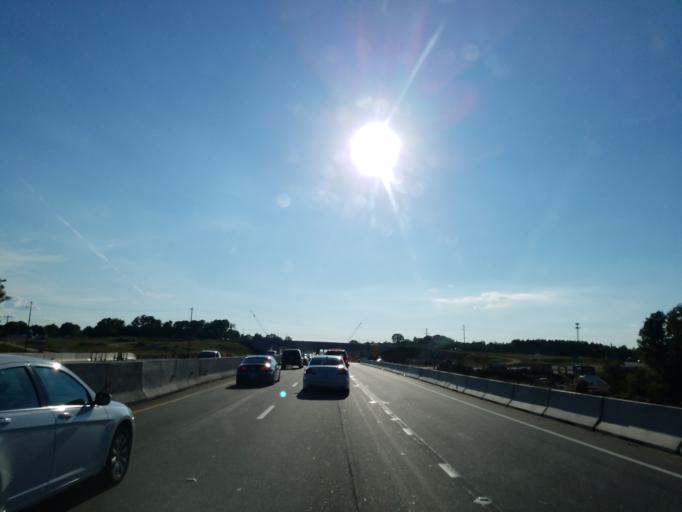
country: US
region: North Carolina
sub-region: Cabarrus County
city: Kannapolis
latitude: 35.4470
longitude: -80.6056
